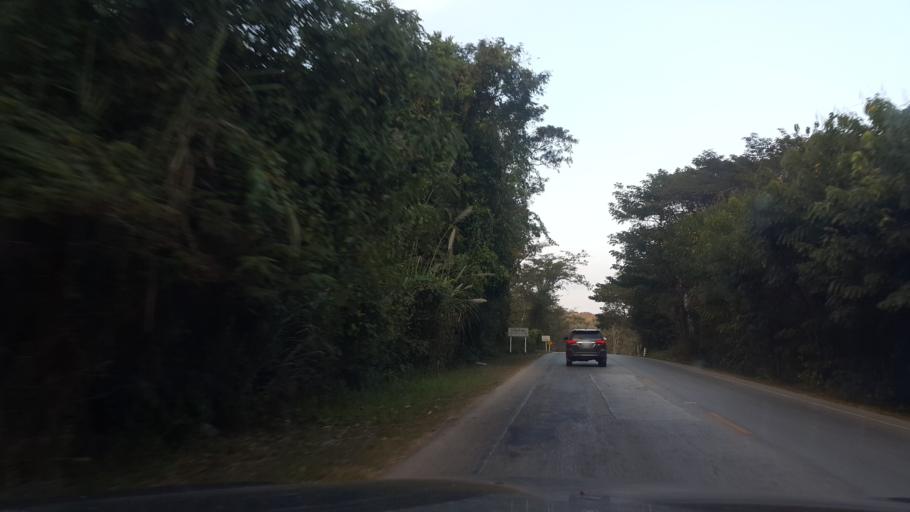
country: TH
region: Loei
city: Loei
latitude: 17.4692
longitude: 101.5961
